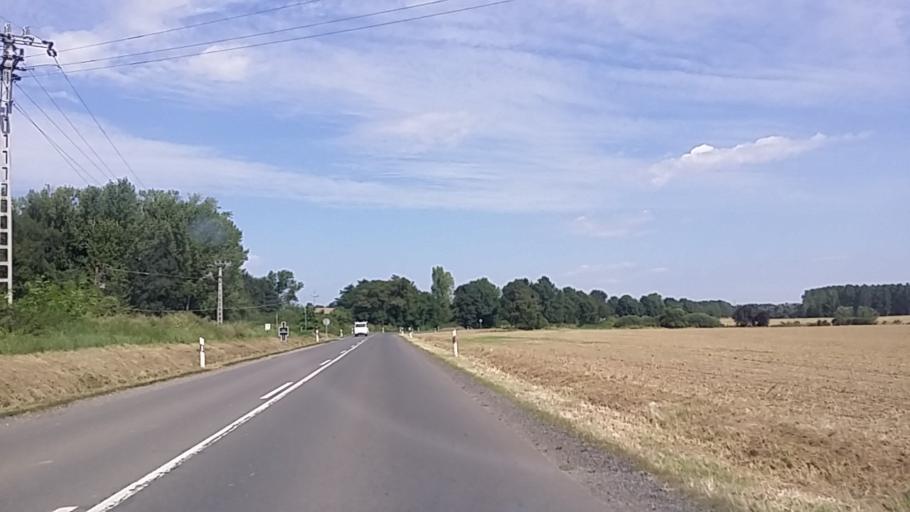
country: HU
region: Baranya
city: Sasd
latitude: 46.2699
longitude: 18.1038
